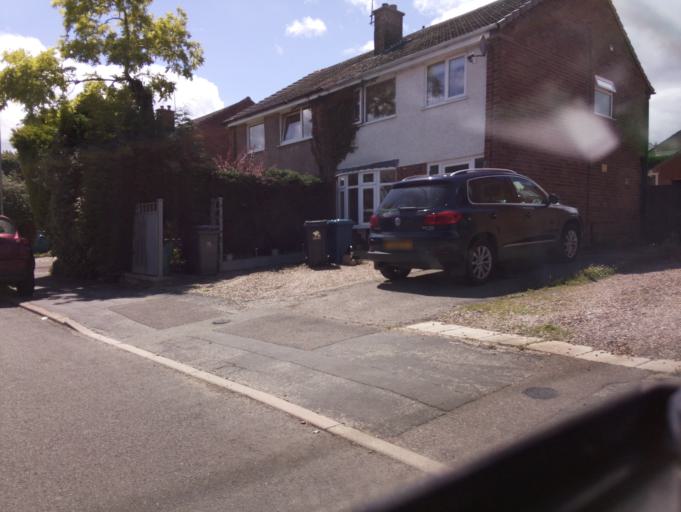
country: GB
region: England
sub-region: Nottinghamshire
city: Cotgrave
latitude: 52.8748
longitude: -1.0832
